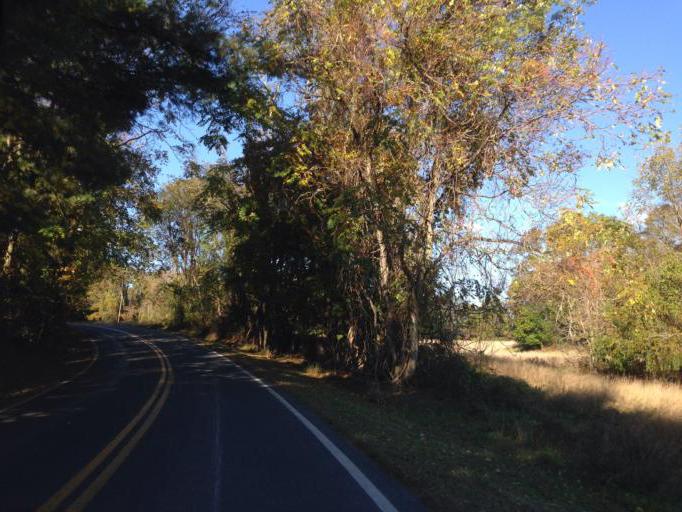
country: US
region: Maryland
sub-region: Carroll County
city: Sykesville
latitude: 39.3367
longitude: -77.0044
